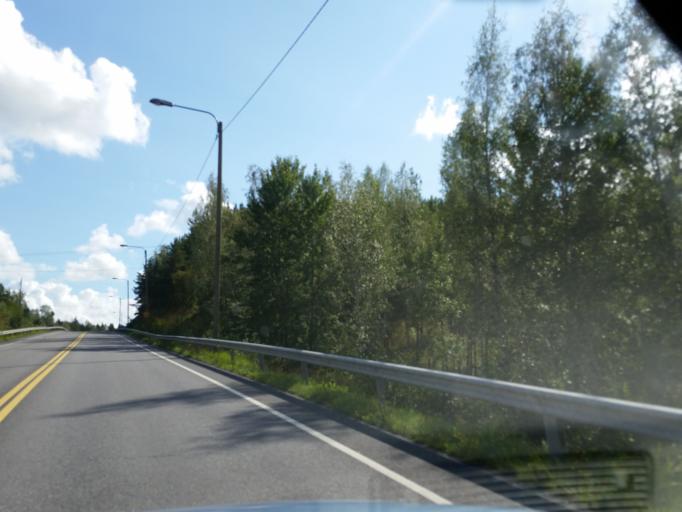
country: FI
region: Varsinais-Suomi
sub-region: Turku
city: Kaarina
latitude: 60.3552
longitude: 22.3582
